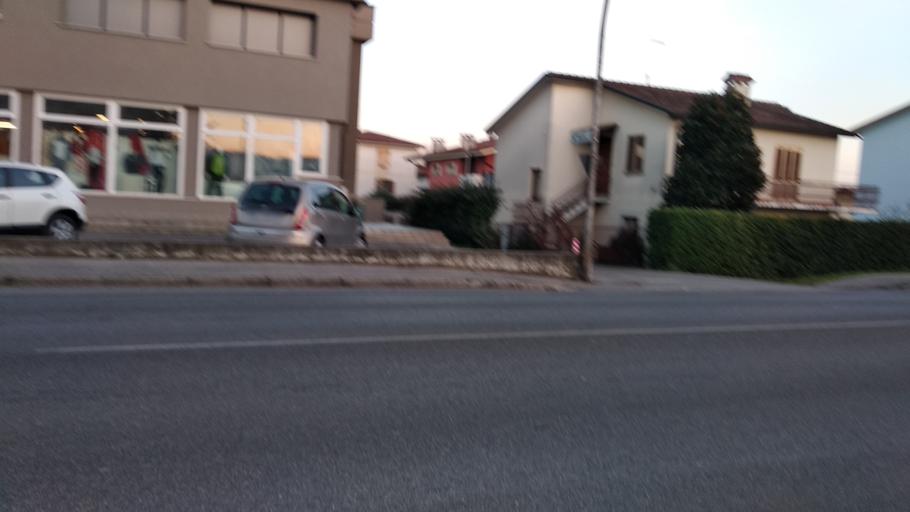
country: IT
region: Veneto
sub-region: Provincia di Vicenza
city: Motta
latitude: 45.5958
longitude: 11.4964
